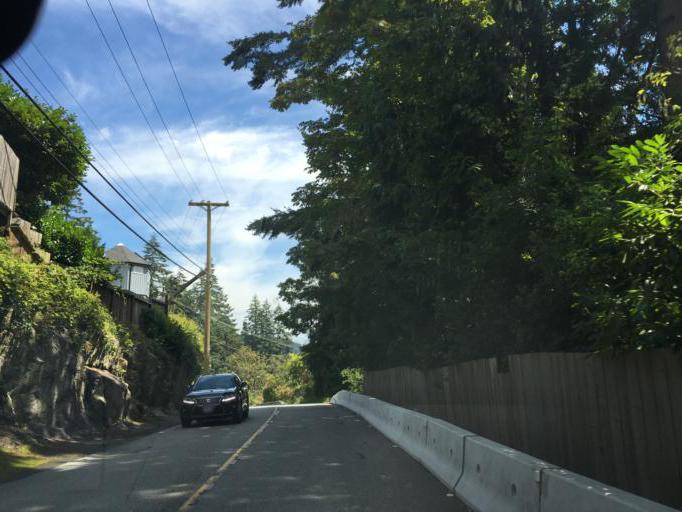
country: CA
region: British Columbia
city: West Vancouver
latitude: 49.3411
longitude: -123.2512
